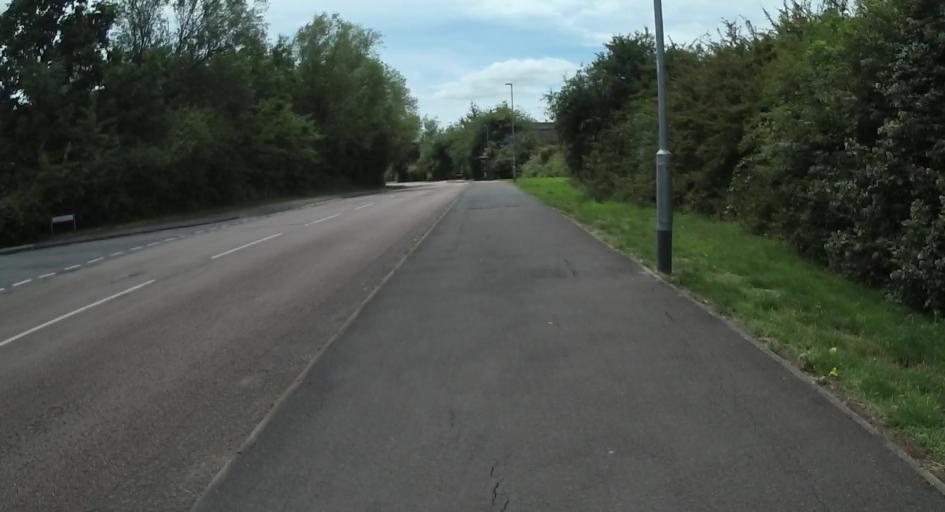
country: GB
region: England
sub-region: Wokingham
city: Lower Earley
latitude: 51.4224
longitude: -0.9294
